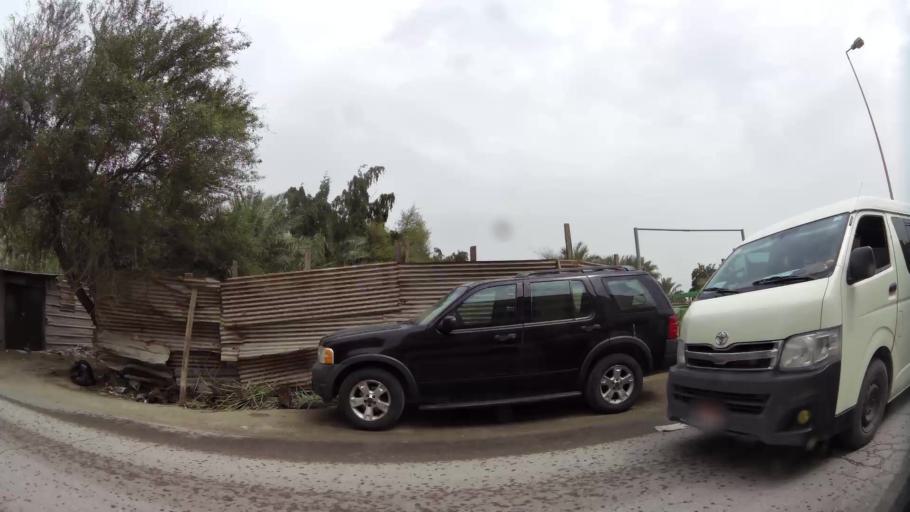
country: BH
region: Northern
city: Ar Rifa'
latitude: 26.1352
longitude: 50.5891
